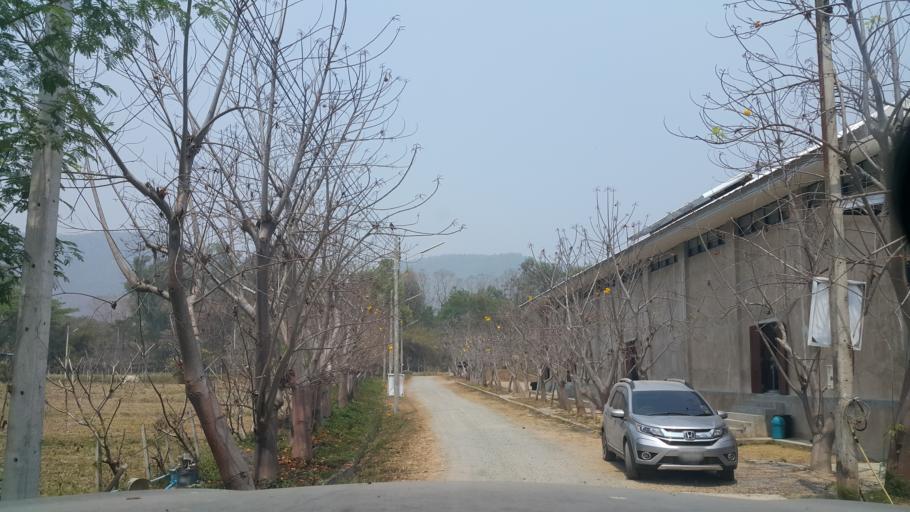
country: TH
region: Chiang Mai
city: Mae On
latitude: 18.7412
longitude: 99.2149
